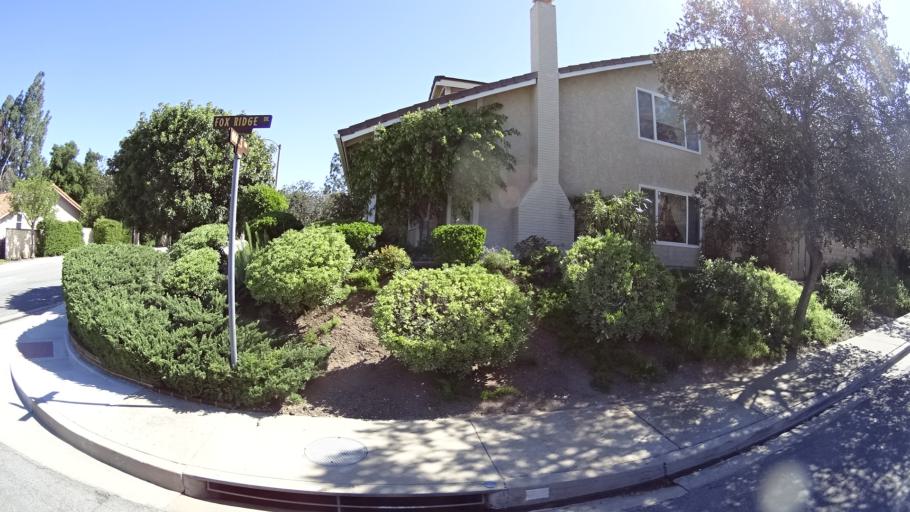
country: US
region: California
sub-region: Ventura County
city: Thousand Oaks
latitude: 34.1737
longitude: -118.8738
